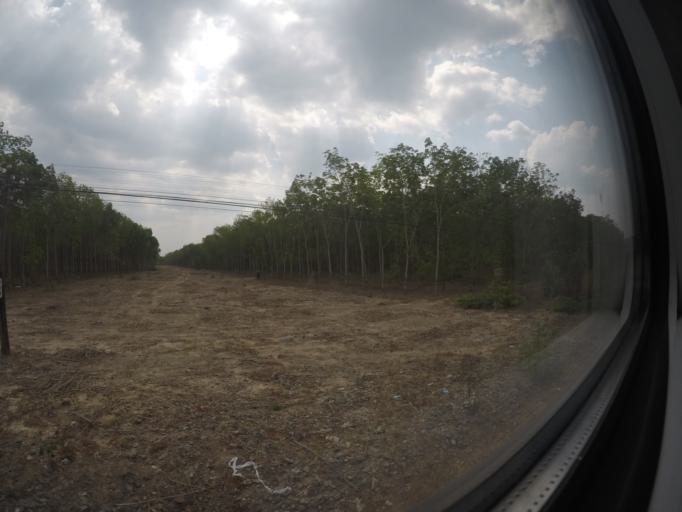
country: VN
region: Binh Thuan
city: Tanh Linh
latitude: 10.9569
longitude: 107.6471
